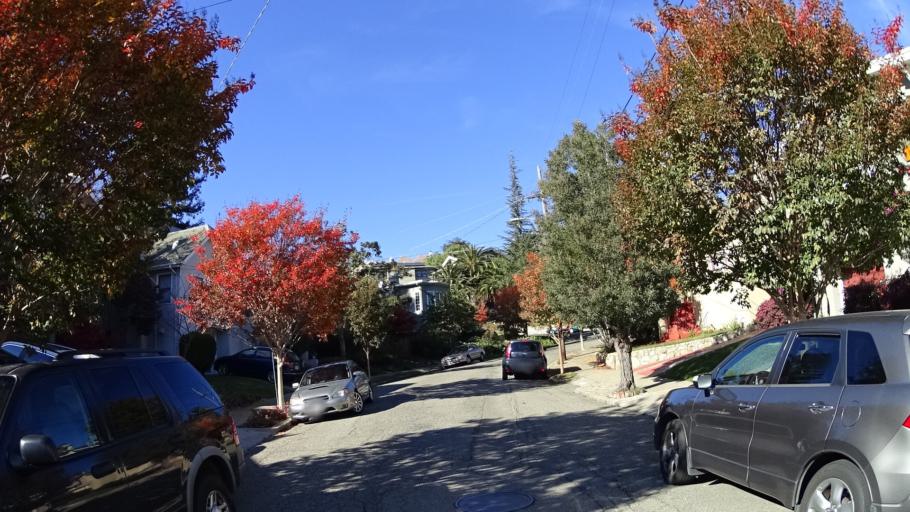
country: US
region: California
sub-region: Alameda County
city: Piedmont
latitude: 37.8150
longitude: -122.2399
